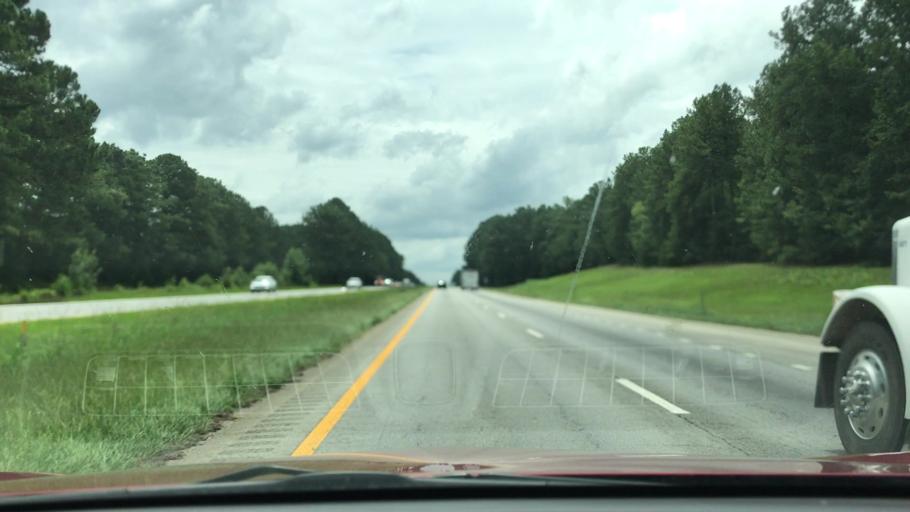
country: US
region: South Carolina
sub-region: Newberry County
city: Newberry
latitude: 34.3763
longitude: -81.6775
